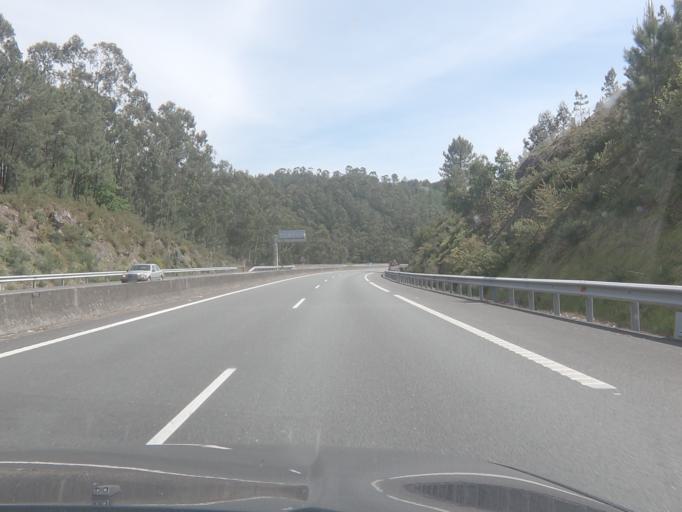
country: ES
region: Galicia
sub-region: Provincia de Pontevedra
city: Portas
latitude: 42.5907
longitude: -8.6770
